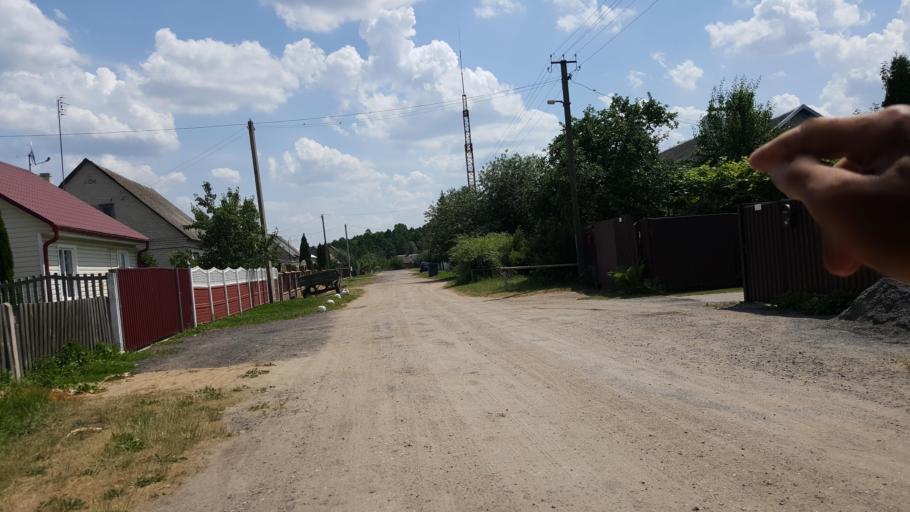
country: BY
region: Brest
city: Kamyanyets
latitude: 52.4025
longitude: 23.7905
